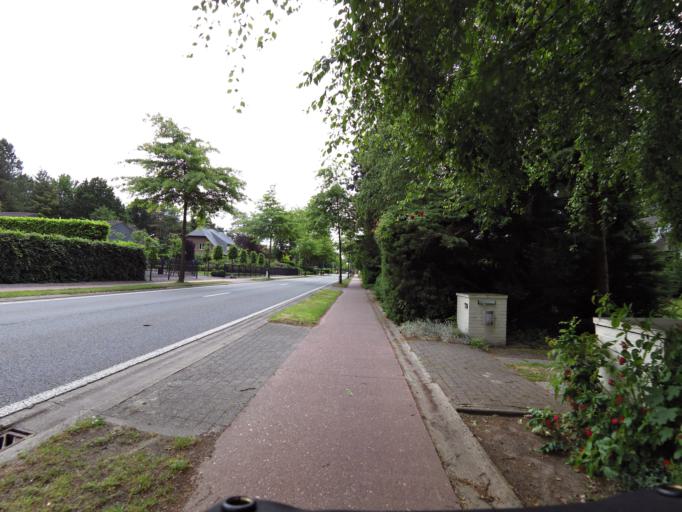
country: BE
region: Flanders
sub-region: Provincie Antwerpen
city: Hoogstraten
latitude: 51.4845
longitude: 4.7952
